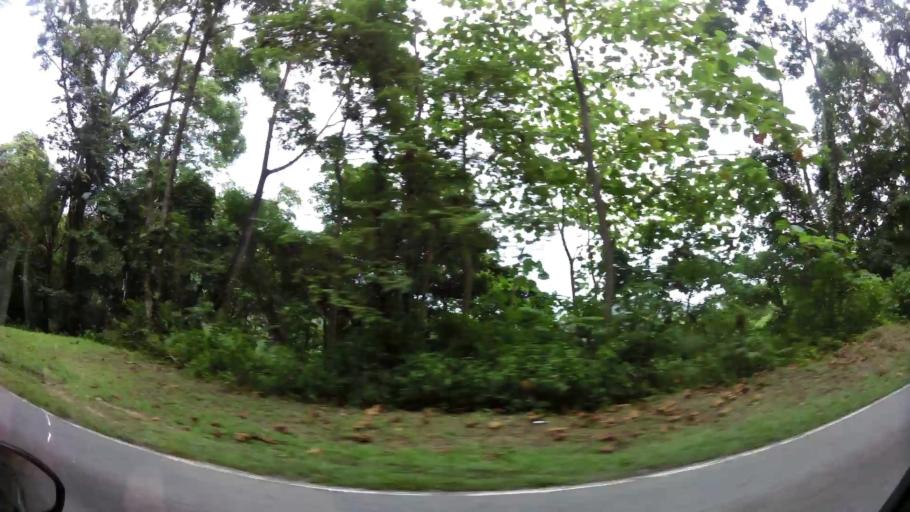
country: TT
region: Diego Martin
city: Petit Valley
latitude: 10.7407
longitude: -61.4943
